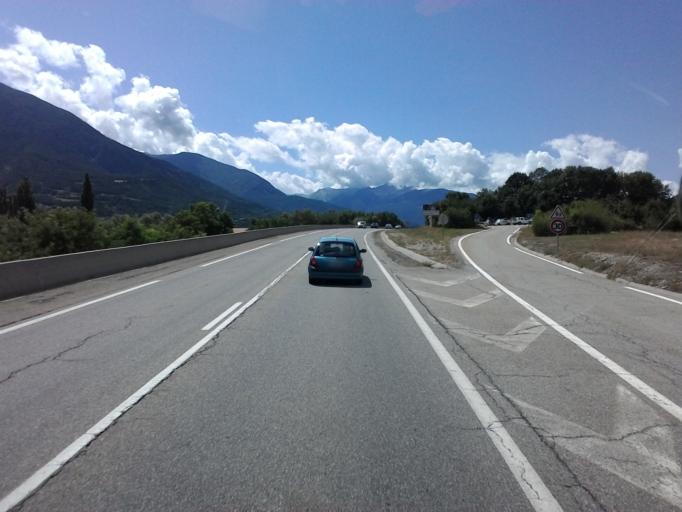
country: FR
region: Provence-Alpes-Cote d'Azur
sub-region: Departement des Hautes-Alpes
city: Embrun
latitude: 44.6175
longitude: 6.5329
